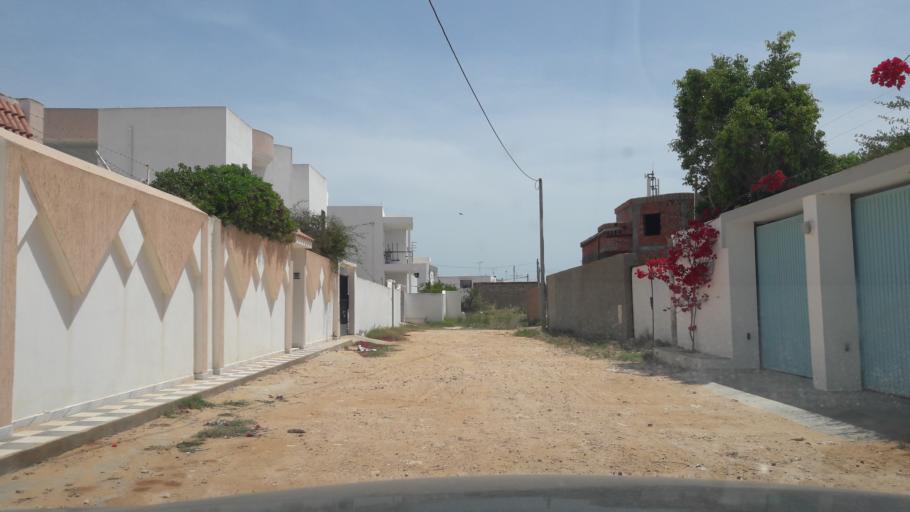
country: TN
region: Safaqis
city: Sfax
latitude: 34.7751
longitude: 10.7553
